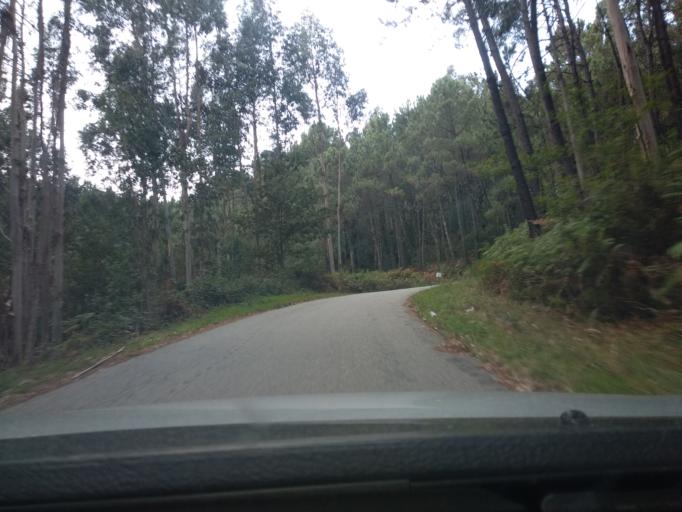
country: ES
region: Galicia
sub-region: Provincia de Pontevedra
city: Moana
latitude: 42.2964
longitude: -8.6948
